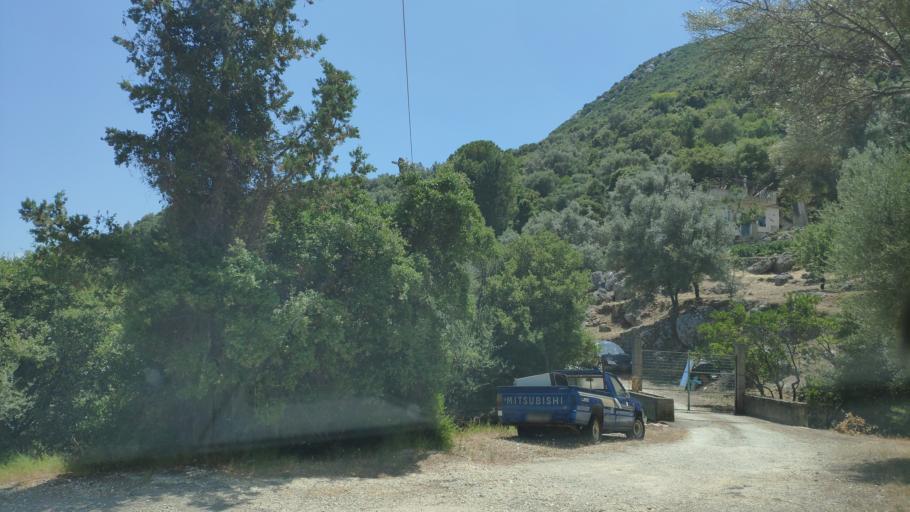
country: GR
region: Ionian Islands
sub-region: Lefkada
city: Nidri
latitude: 38.7527
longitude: 20.7144
